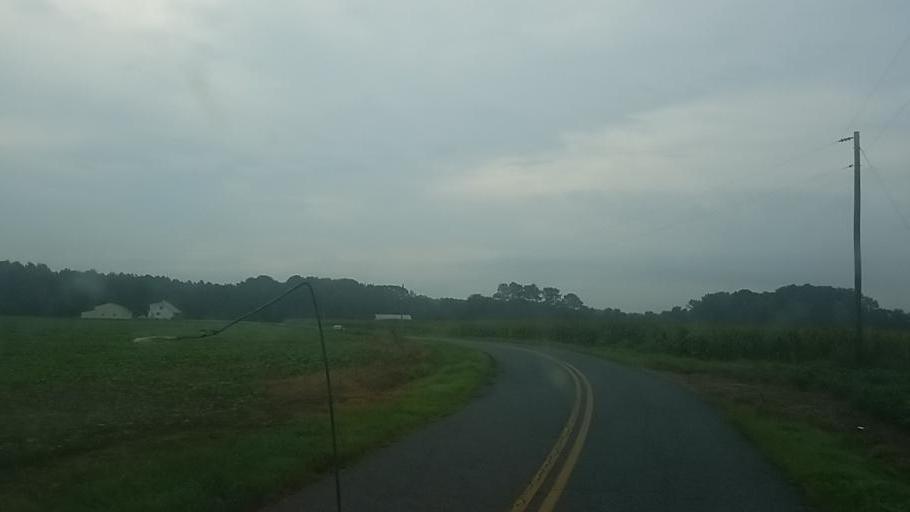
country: US
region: Maryland
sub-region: Wicomico County
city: Pittsville
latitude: 38.4224
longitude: -75.3175
